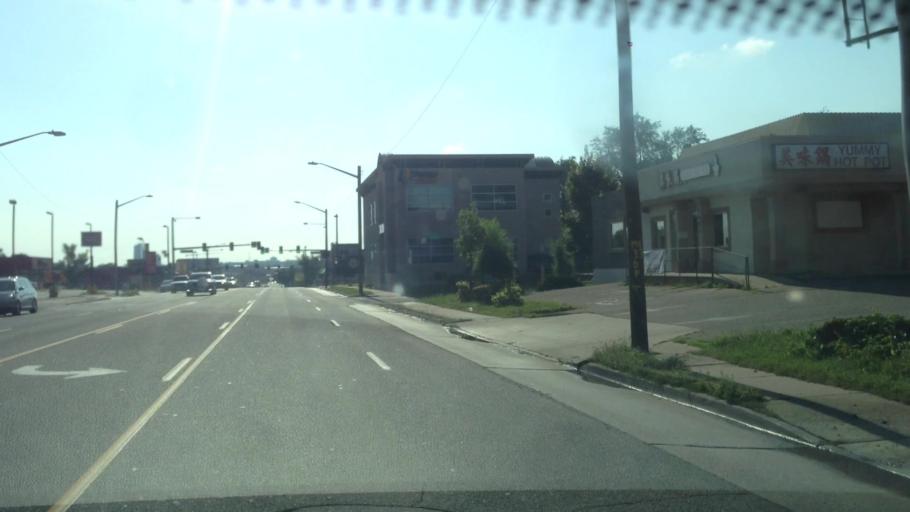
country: US
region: Colorado
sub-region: Denver County
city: Denver
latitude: 39.7112
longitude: -105.0176
